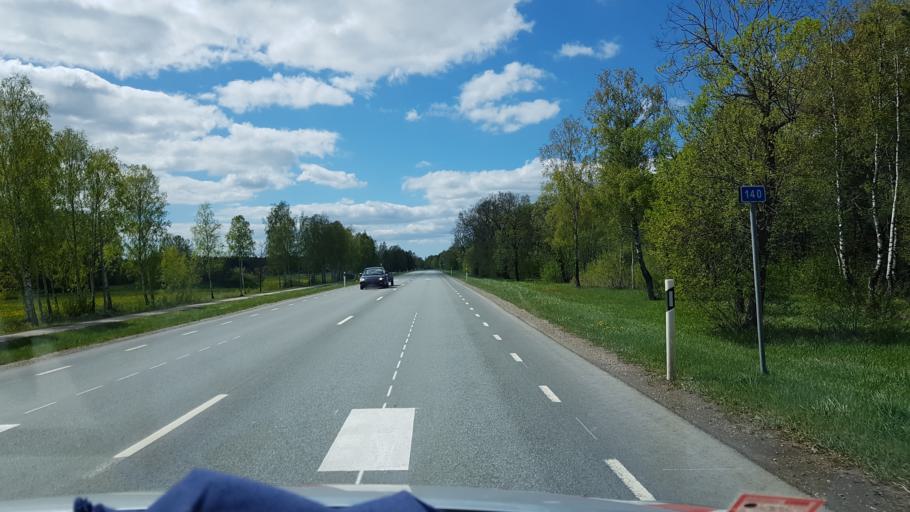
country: EE
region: Saare
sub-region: Kuressaare linn
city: Kuressaare
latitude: 58.2759
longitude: 22.5294
